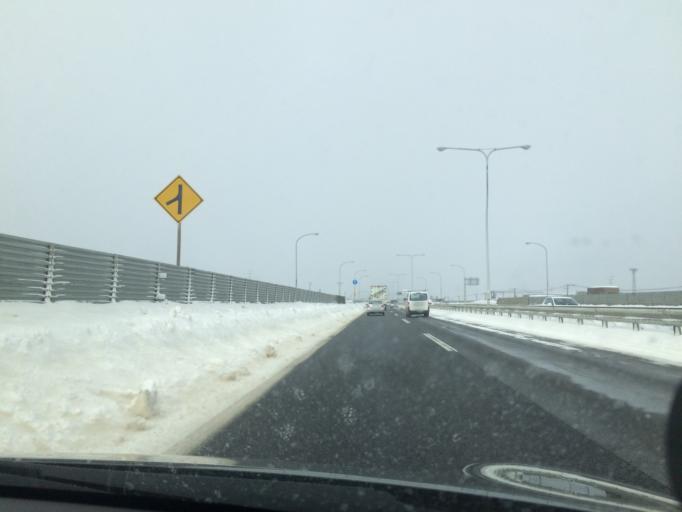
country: JP
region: Hokkaido
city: Sapporo
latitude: 43.0412
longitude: 141.4380
